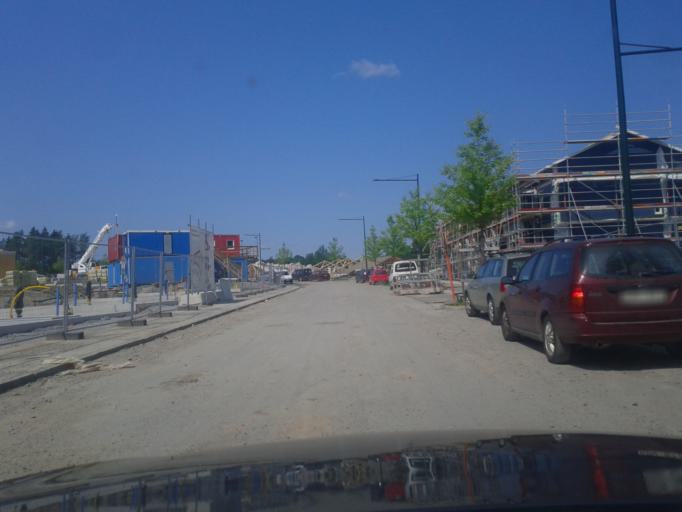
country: SE
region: Stockholm
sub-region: Taby Kommun
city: Taby
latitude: 59.4739
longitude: 18.1299
